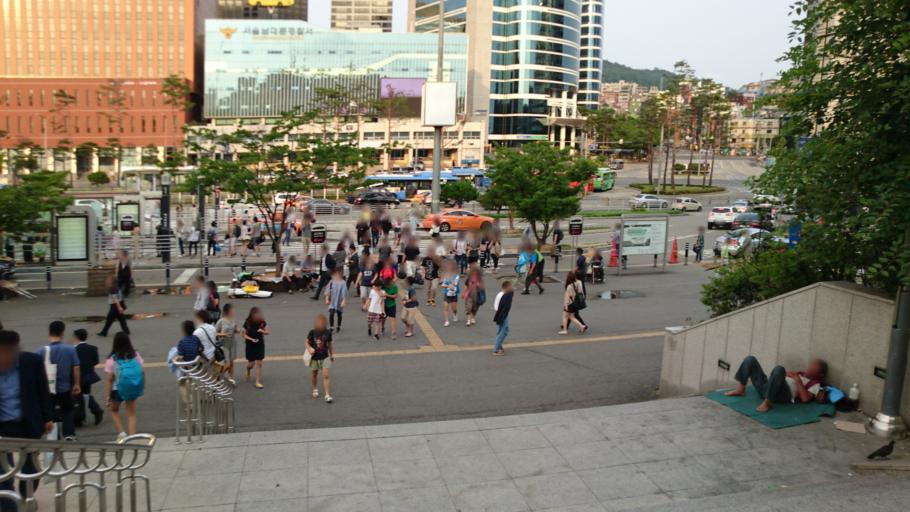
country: KR
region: Seoul
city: Seoul
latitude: 37.5547
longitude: 126.9720
